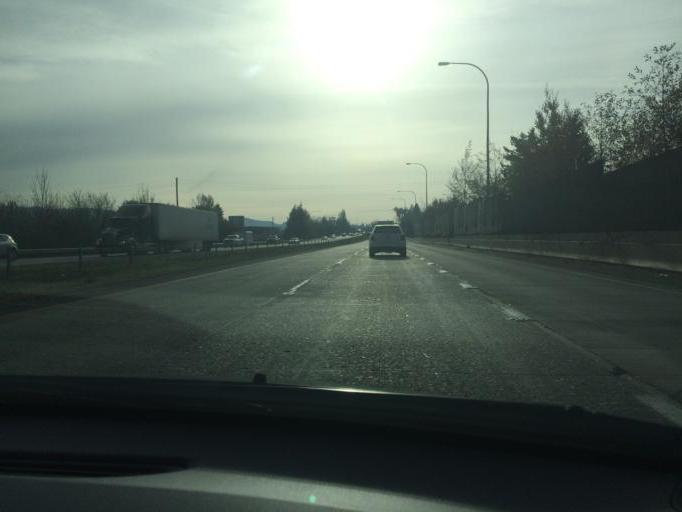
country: US
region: Washington
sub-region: Whatcom County
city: Bellingham
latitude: 48.7520
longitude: -122.4632
